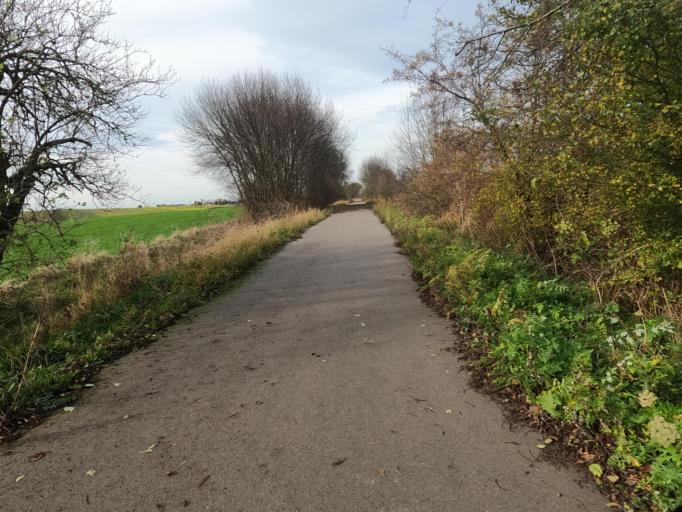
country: PL
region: Pomeranian Voivodeship
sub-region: Powiat starogardzki
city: Starogard Gdanski
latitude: 53.9747
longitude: 18.4990
